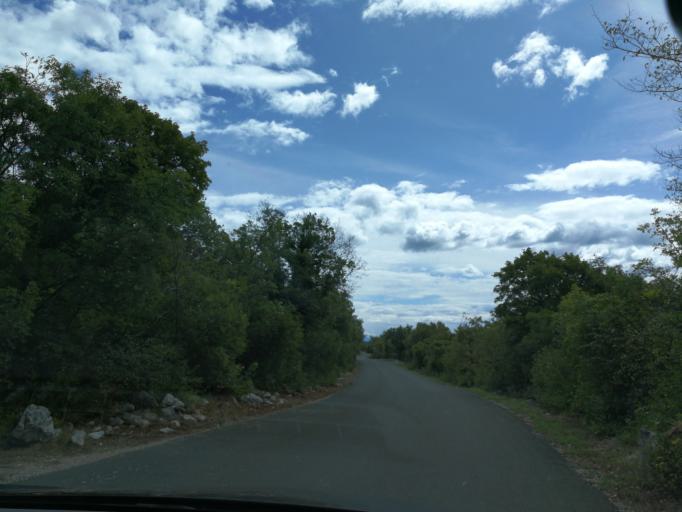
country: HR
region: Primorsko-Goranska
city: Omisalj
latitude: 45.2034
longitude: 14.5701
